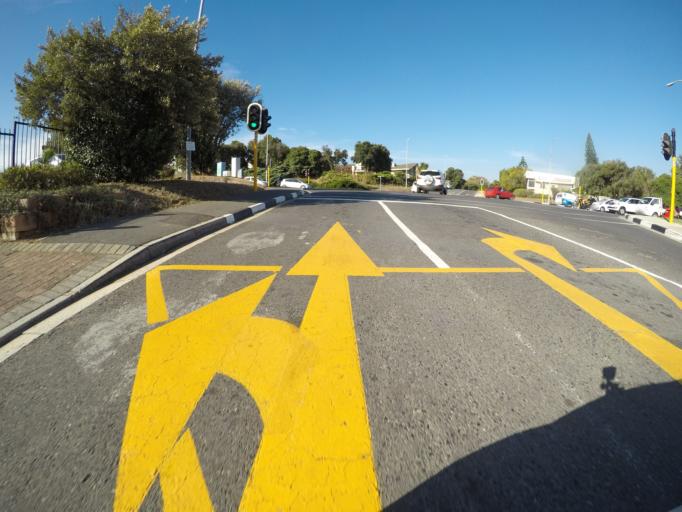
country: ZA
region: Western Cape
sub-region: City of Cape Town
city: Kraaifontein
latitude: -33.8802
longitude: 18.6446
